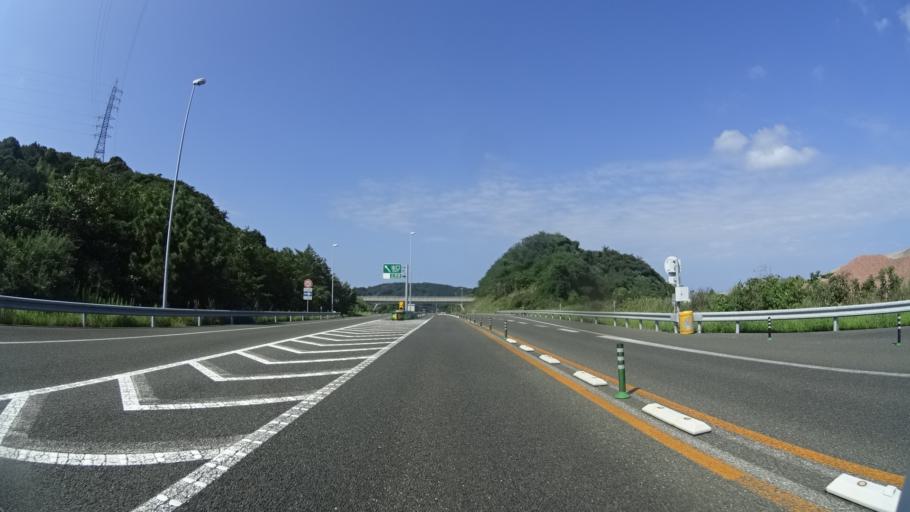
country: JP
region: Shimane
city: Gotsucho
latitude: 34.9714
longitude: 132.1822
